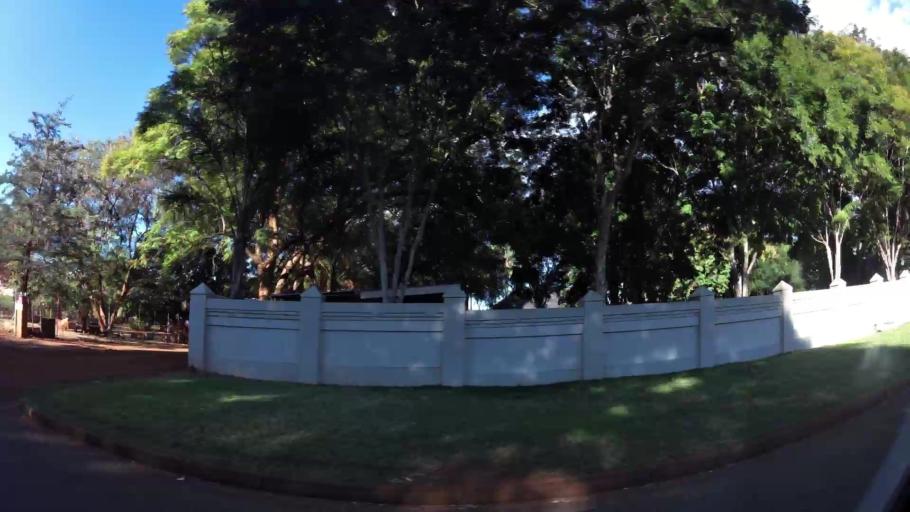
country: ZA
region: Limpopo
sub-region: Waterberg District Municipality
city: Mokopane
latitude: -24.1913
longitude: 29.0056
